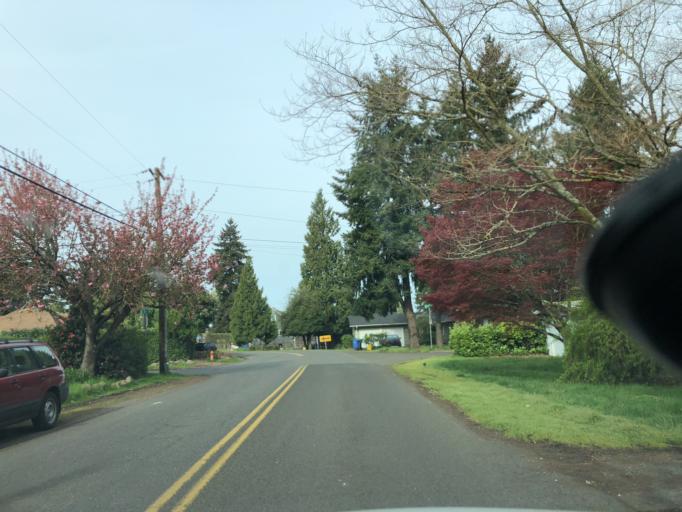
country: US
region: Oregon
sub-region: Multnomah County
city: Portland
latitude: 45.5592
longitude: -122.6144
